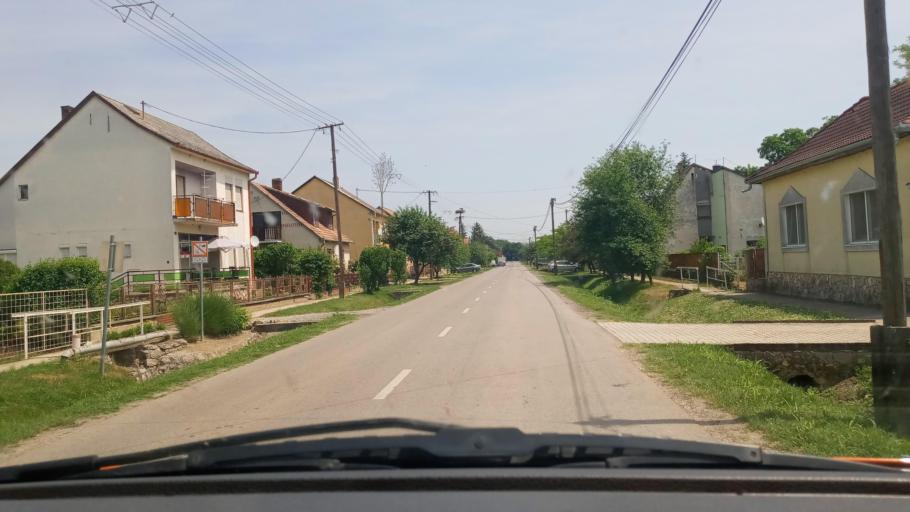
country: HU
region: Baranya
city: Szigetvar
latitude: 45.9659
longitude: 17.7166
